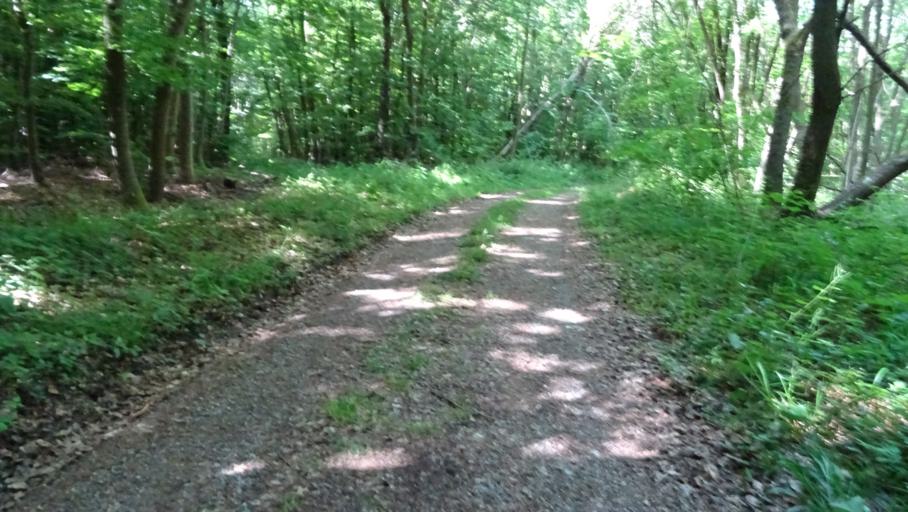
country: DE
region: Baden-Wuerttemberg
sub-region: Karlsruhe Region
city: Obrigheim
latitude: 49.3428
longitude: 9.0871
